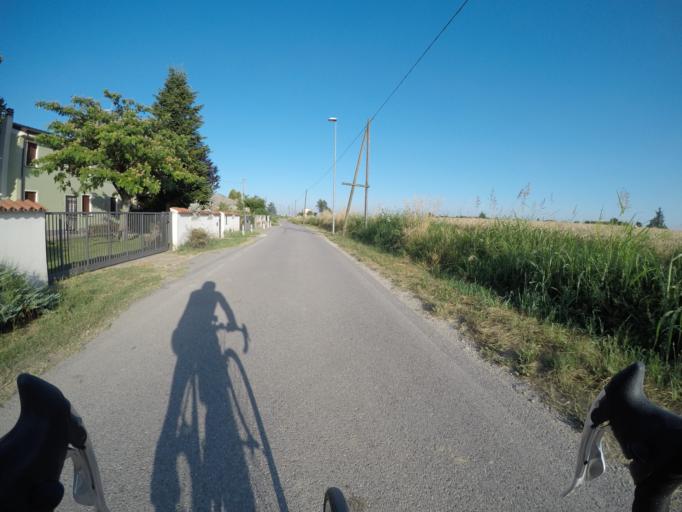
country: IT
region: Veneto
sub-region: Provincia di Rovigo
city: Fratta Polesine
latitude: 45.0288
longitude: 11.6538
